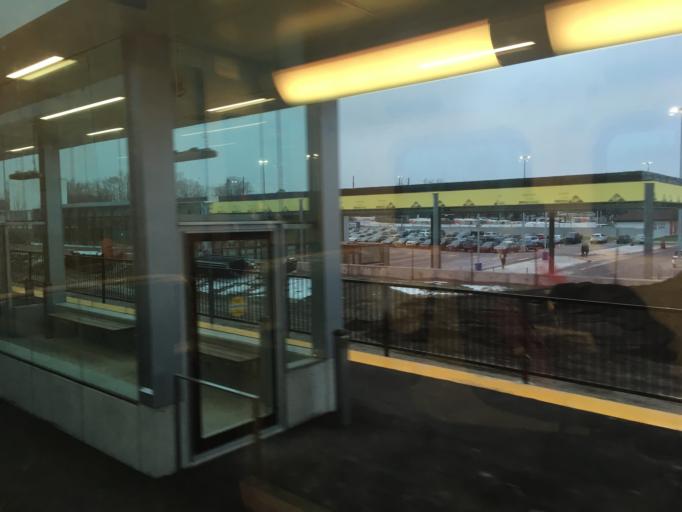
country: CA
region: Ontario
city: Scarborough
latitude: 43.7551
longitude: -79.1981
